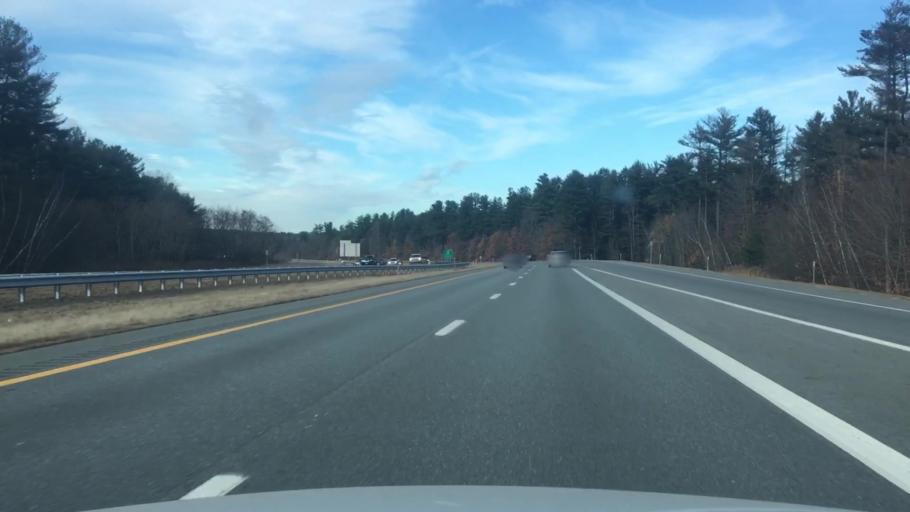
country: US
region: New Hampshire
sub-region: Rockingham County
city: Exeter
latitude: 42.9967
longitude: -70.9309
